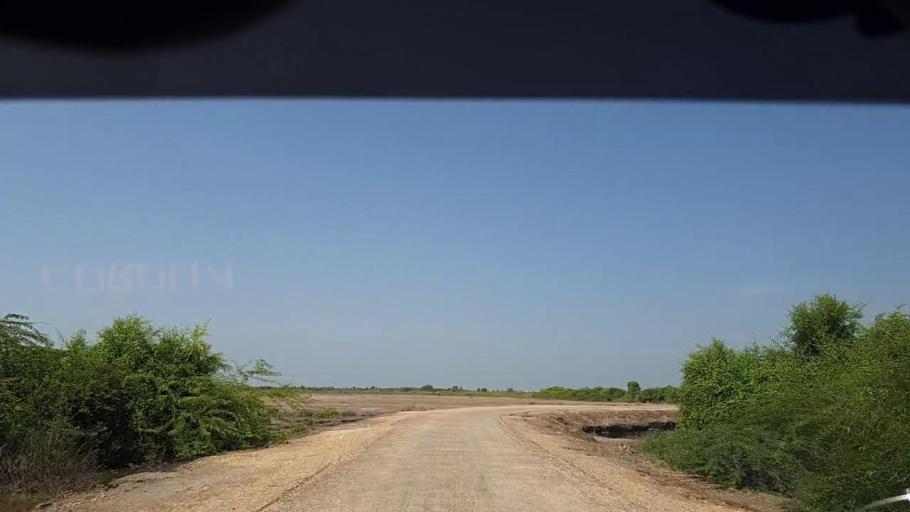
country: PK
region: Sindh
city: Badin
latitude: 24.4573
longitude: 68.7609
